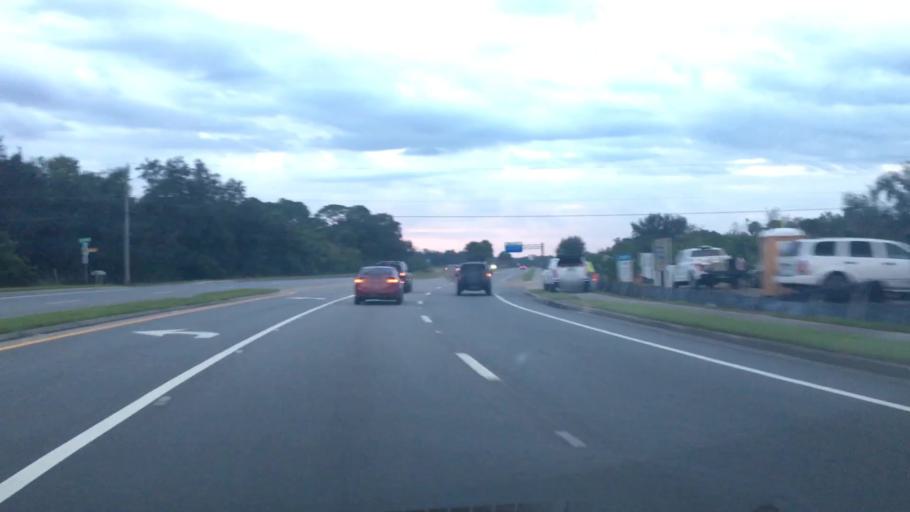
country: US
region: Florida
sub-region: Seminole County
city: Midway
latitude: 28.7812
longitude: -81.2105
